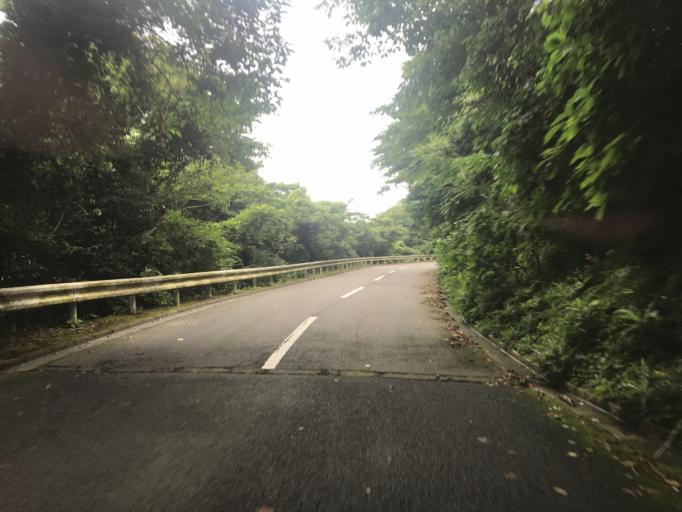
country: JP
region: Shizuoka
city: Ito
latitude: 34.7622
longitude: 139.4158
